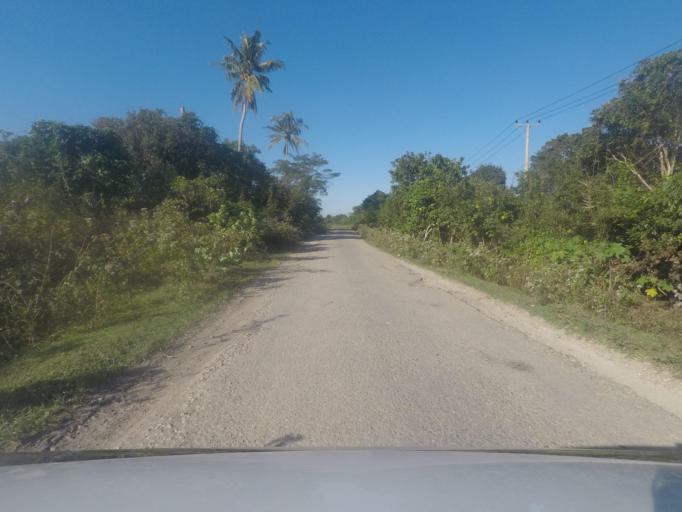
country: TL
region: Lautem
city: Lospalos
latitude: -8.4094
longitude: 127.1672
